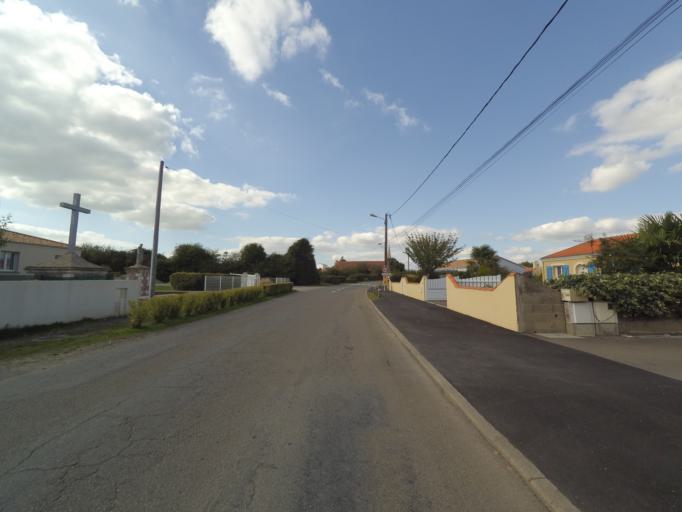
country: FR
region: Pays de la Loire
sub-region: Departement de la Loire-Atlantique
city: Chemere
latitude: 47.1200
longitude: -1.9114
